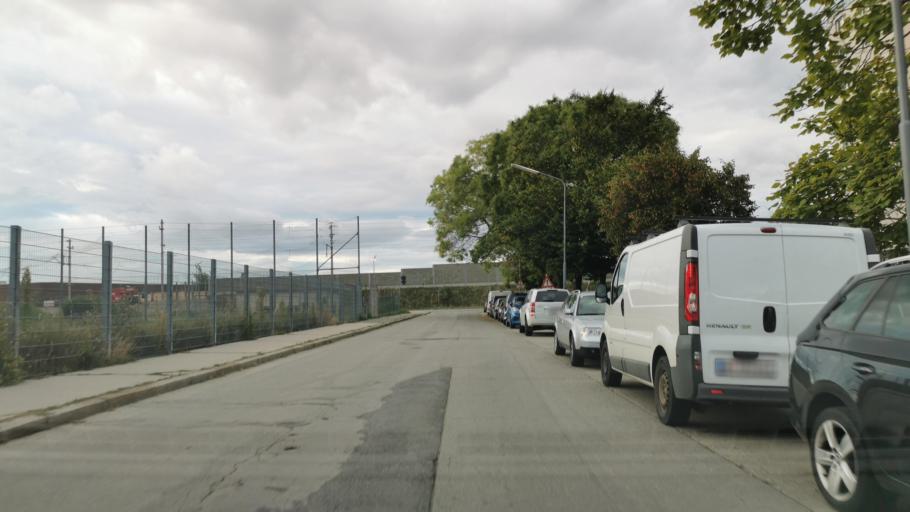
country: AT
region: Lower Austria
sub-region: Politischer Bezirk Wien-Umgebung
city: Gerasdorf bei Wien
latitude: 48.2340
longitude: 16.4723
